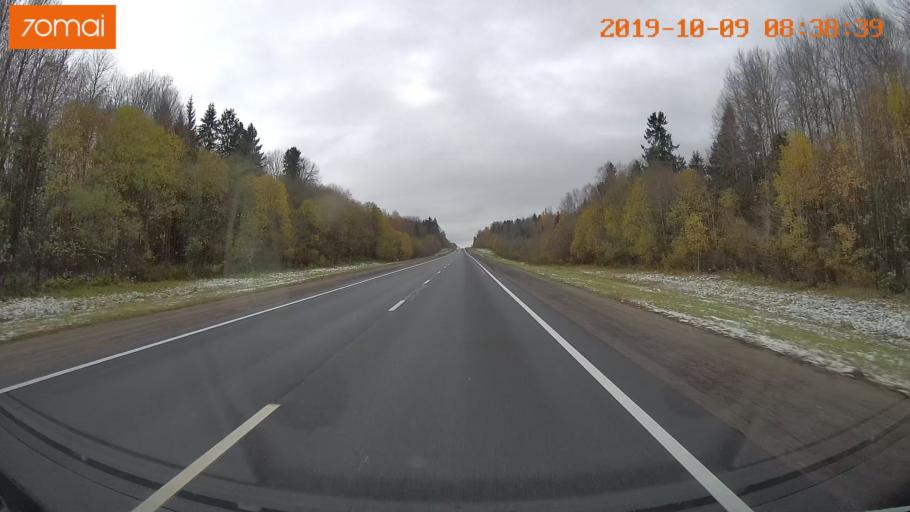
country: RU
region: Vologda
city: Gryazovets
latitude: 58.9598
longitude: 40.1630
